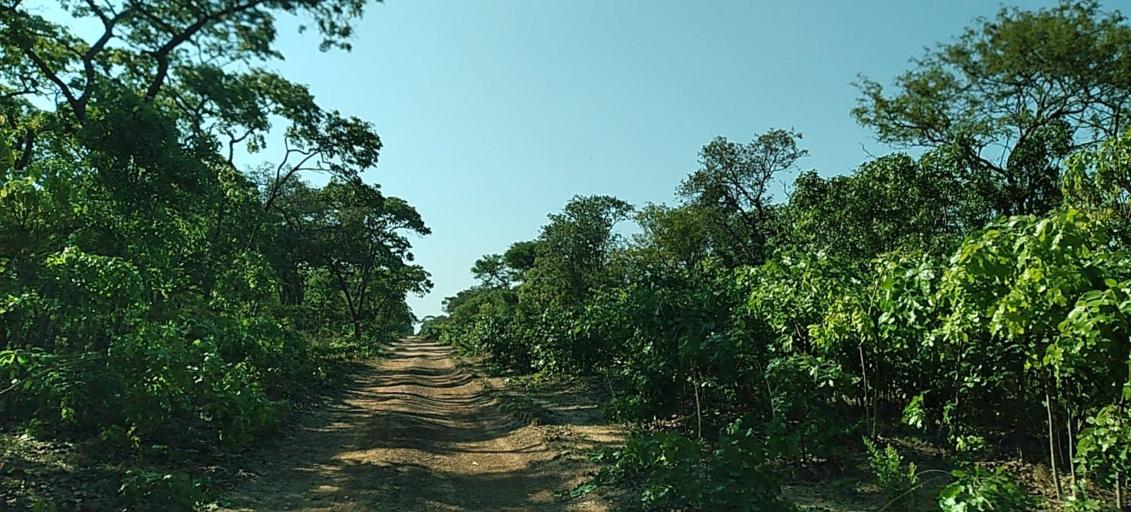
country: ZM
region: Central
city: Mkushi
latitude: -13.4740
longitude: 28.9196
